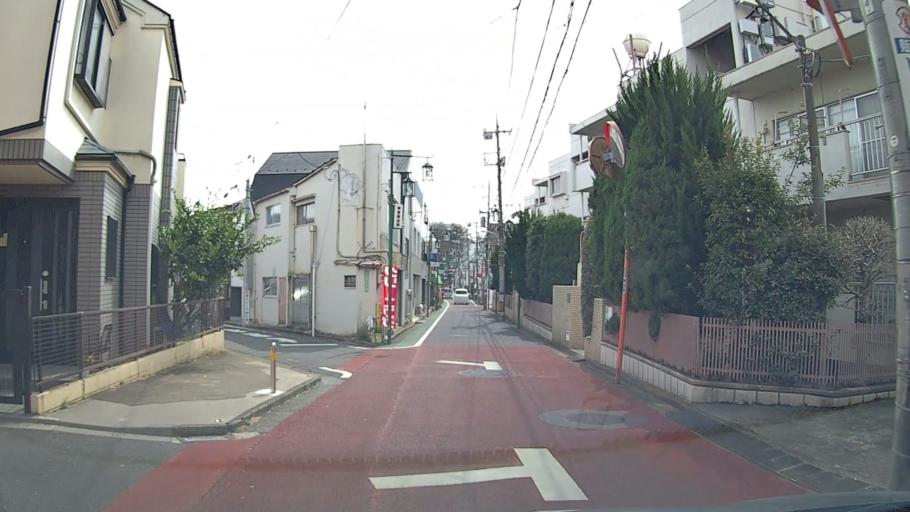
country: JP
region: Saitama
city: Wako
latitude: 35.7507
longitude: 139.6554
